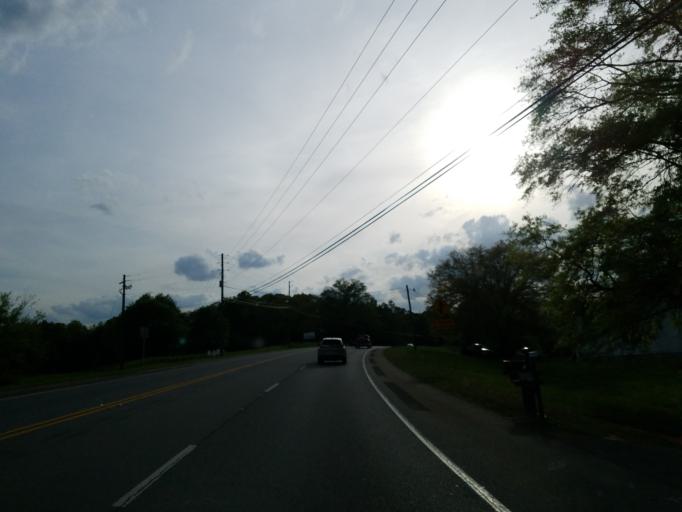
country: US
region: Georgia
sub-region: Cherokee County
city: Ball Ground
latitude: 34.2417
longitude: -84.3854
